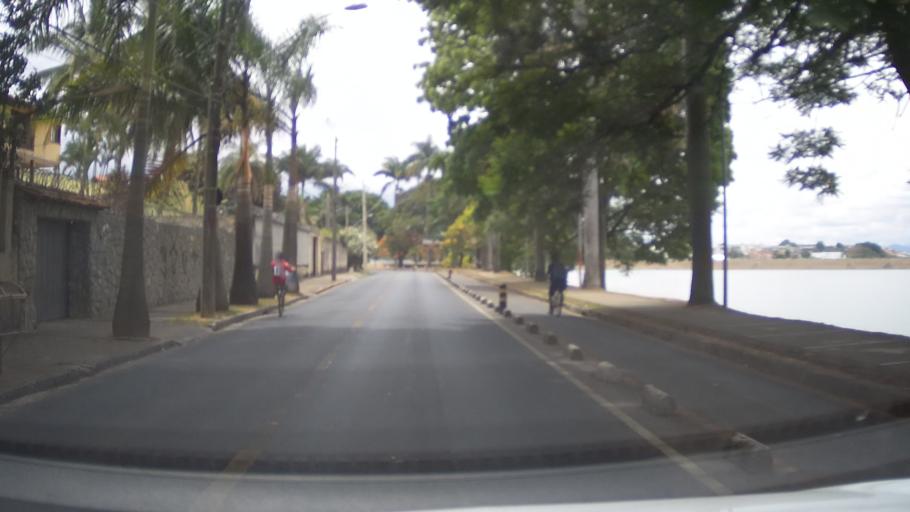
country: BR
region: Minas Gerais
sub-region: Belo Horizonte
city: Belo Horizonte
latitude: -19.8469
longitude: -43.9708
